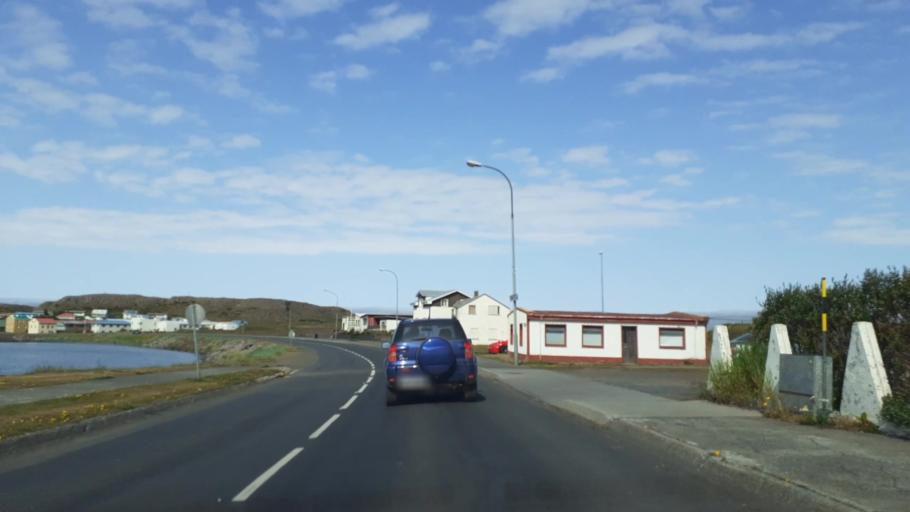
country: IS
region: Northwest
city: Saudarkrokur
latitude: 65.8252
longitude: -20.3074
